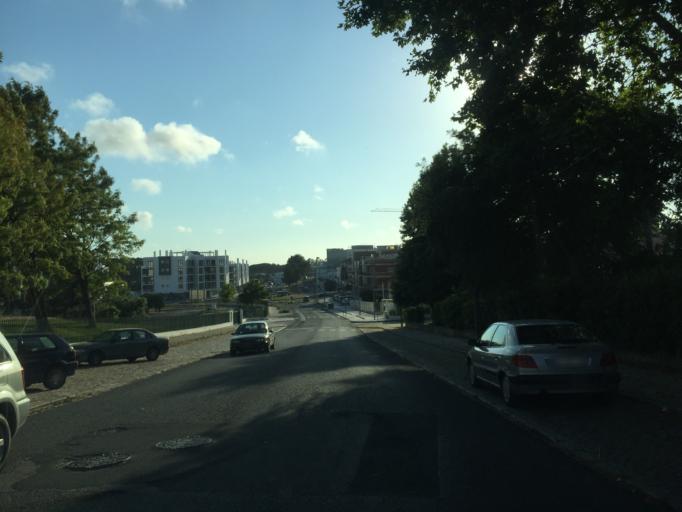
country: PT
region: Leiria
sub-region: Caldas da Rainha
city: Caldas da Rainha
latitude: 39.3980
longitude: -9.1312
